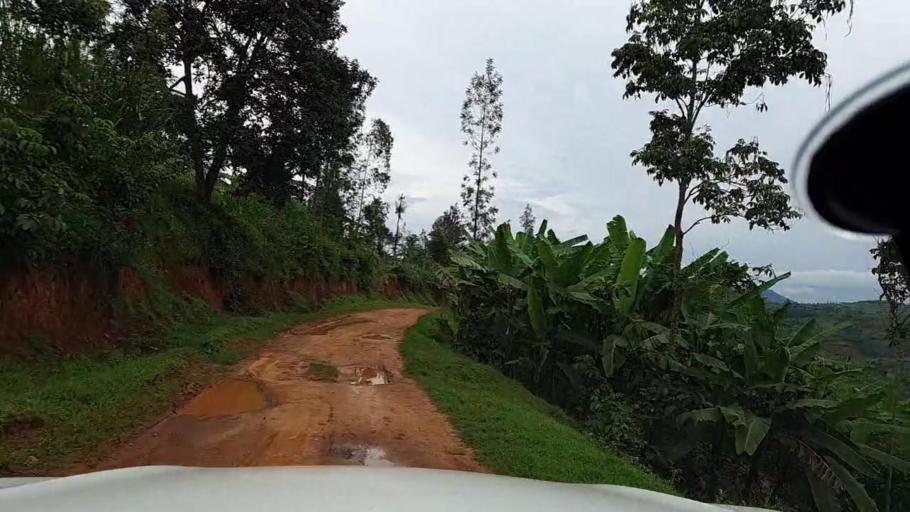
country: RW
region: Southern Province
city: Gitarama
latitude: -2.0891
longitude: 29.6362
